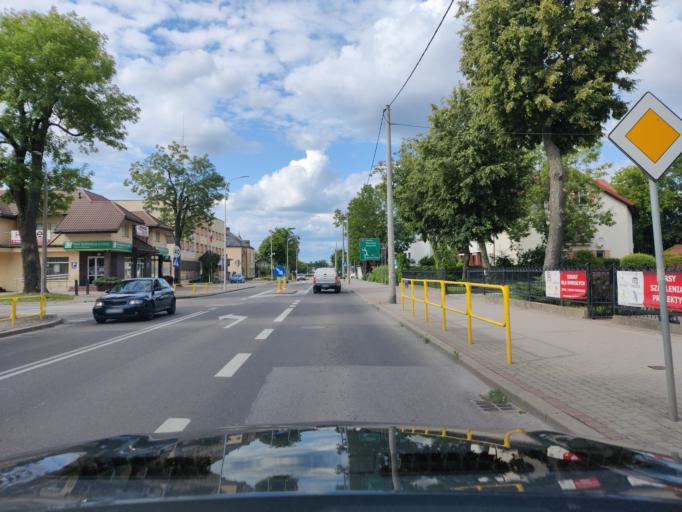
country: PL
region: Podlasie
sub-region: Powiat zambrowski
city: Zambrow
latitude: 52.9783
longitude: 22.2451
